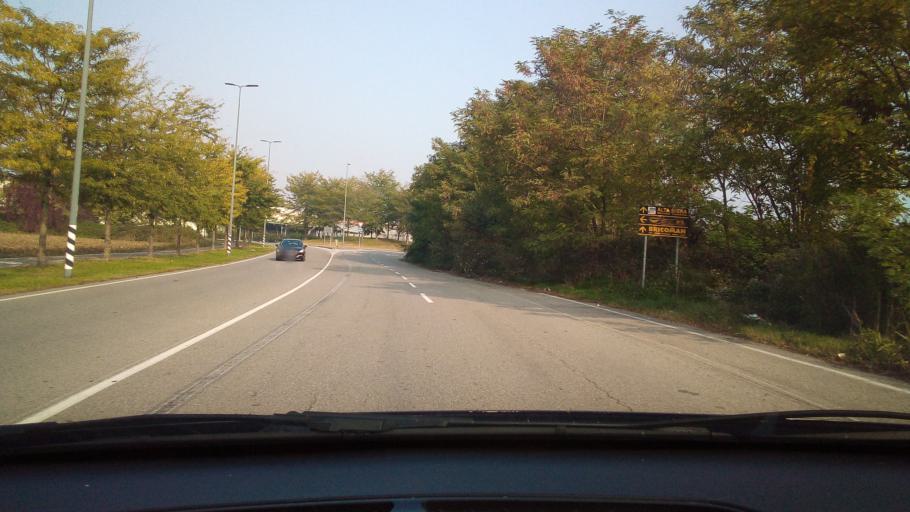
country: IT
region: Lombardy
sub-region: Citta metropolitana di Milano
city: Novegro-Tregarezzo-San Felice
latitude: 45.4828
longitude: 9.2639
